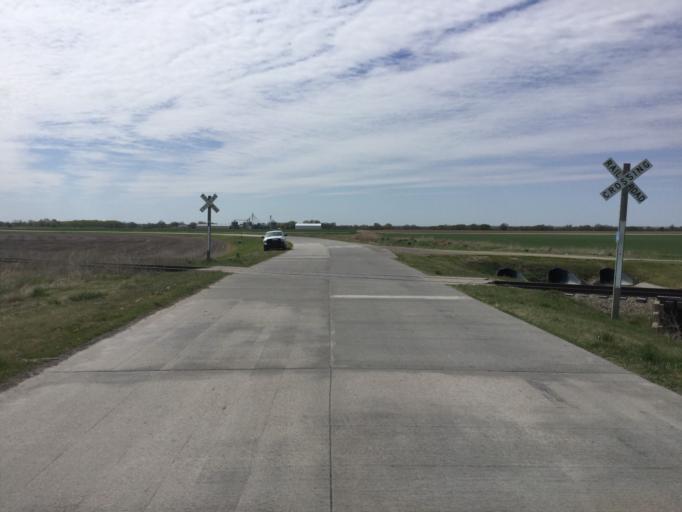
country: US
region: Kansas
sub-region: Osborne County
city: Osborne
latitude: 39.5063
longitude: -98.5630
